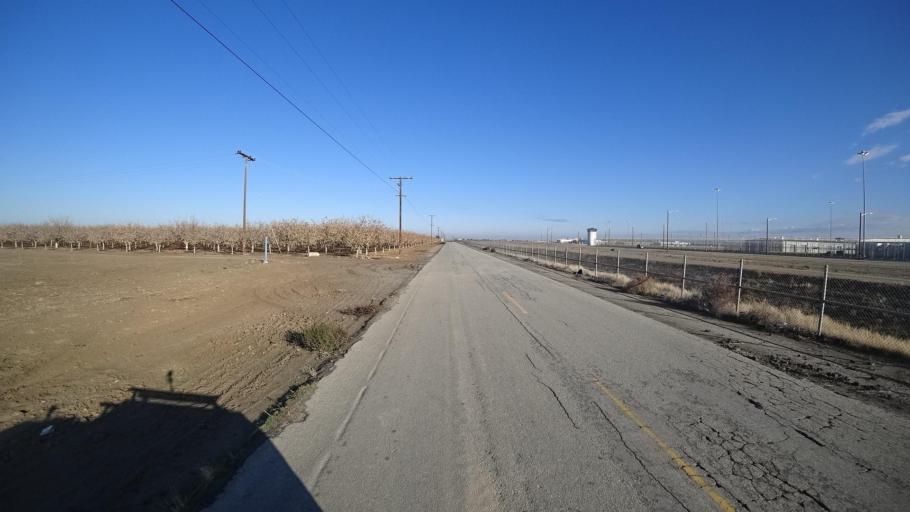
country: US
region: California
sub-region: Kern County
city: Delano
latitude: 35.7683
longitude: -119.3298
